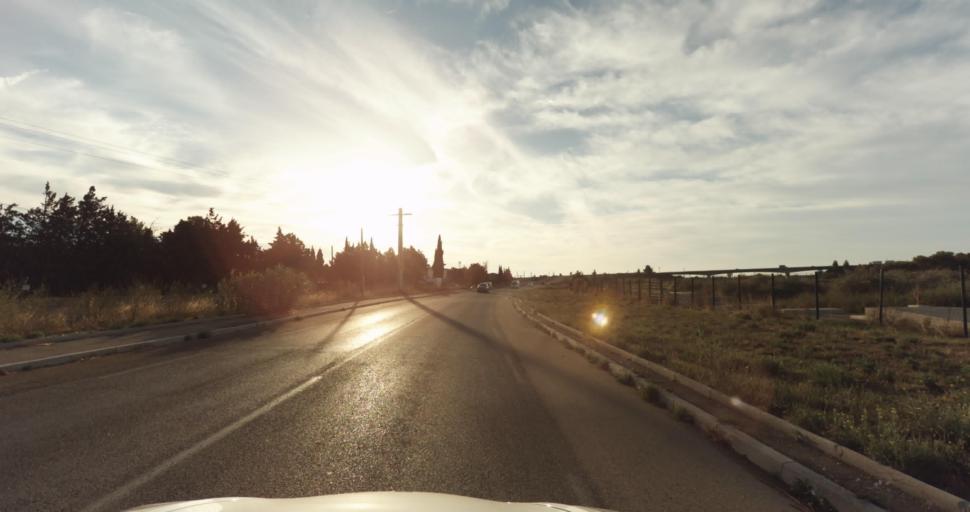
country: FR
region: Provence-Alpes-Cote d'Azur
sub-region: Departement des Bouches-du-Rhone
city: Miramas
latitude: 43.5872
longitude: 4.9829
